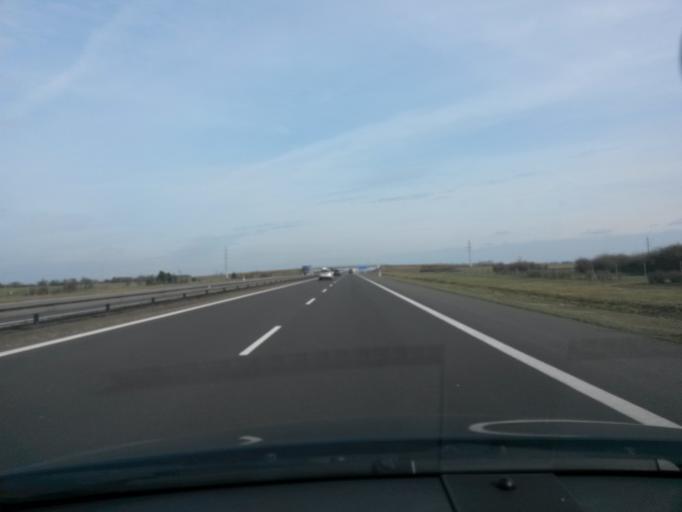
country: PL
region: Greater Poland Voivodeship
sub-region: Powiat poznanski
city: Swarzedz
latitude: 52.3331
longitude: 17.0722
